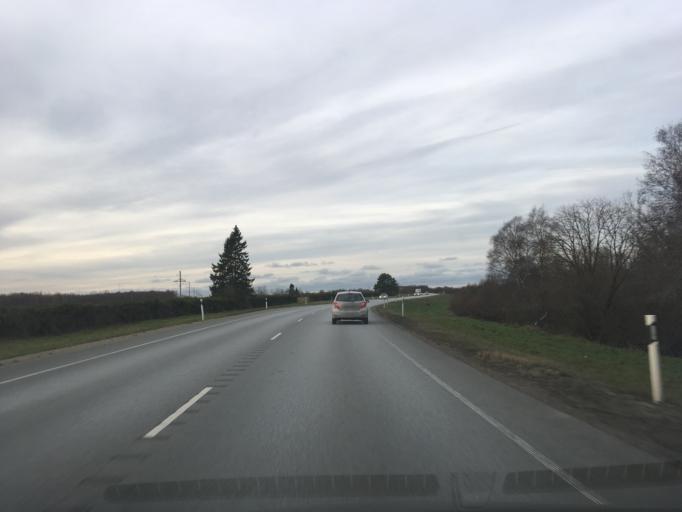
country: EE
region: Ida-Virumaa
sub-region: Kivioli linn
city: Kivioli
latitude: 59.4180
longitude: 26.9739
